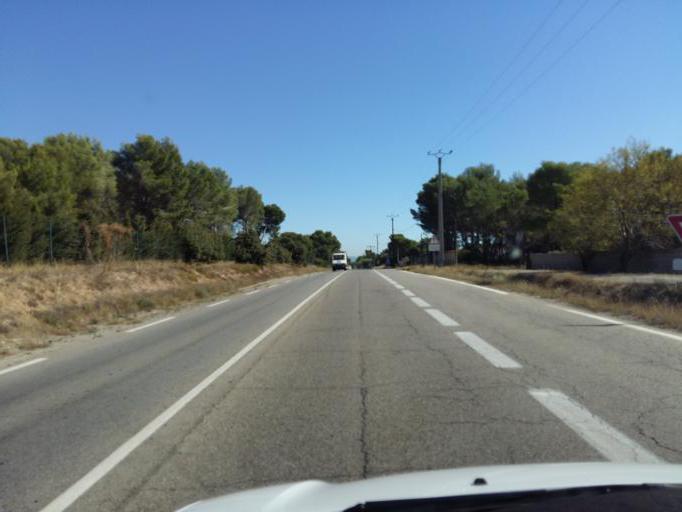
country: FR
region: Provence-Alpes-Cote d'Azur
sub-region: Departement du Vaucluse
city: Merindol
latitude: 43.7535
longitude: 5.1902
